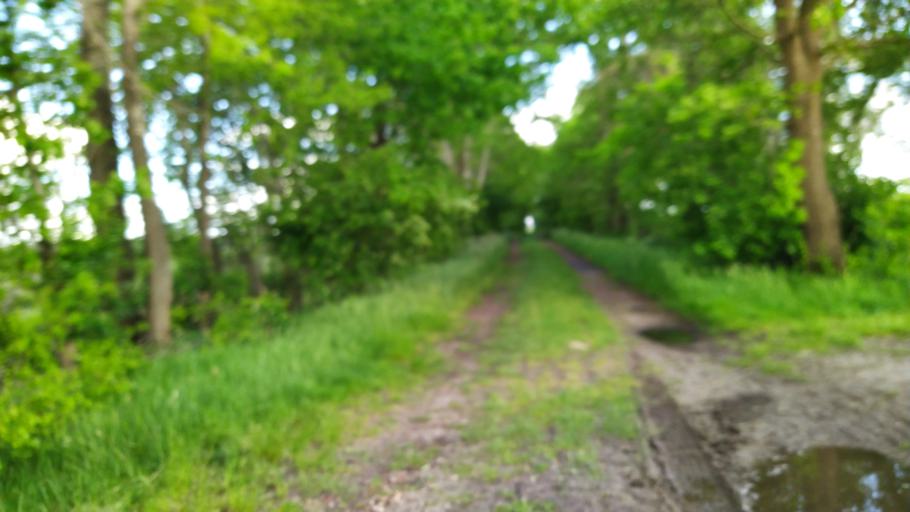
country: DE
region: Lower Saxony
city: Farven
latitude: 53.4540
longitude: 9.2945
